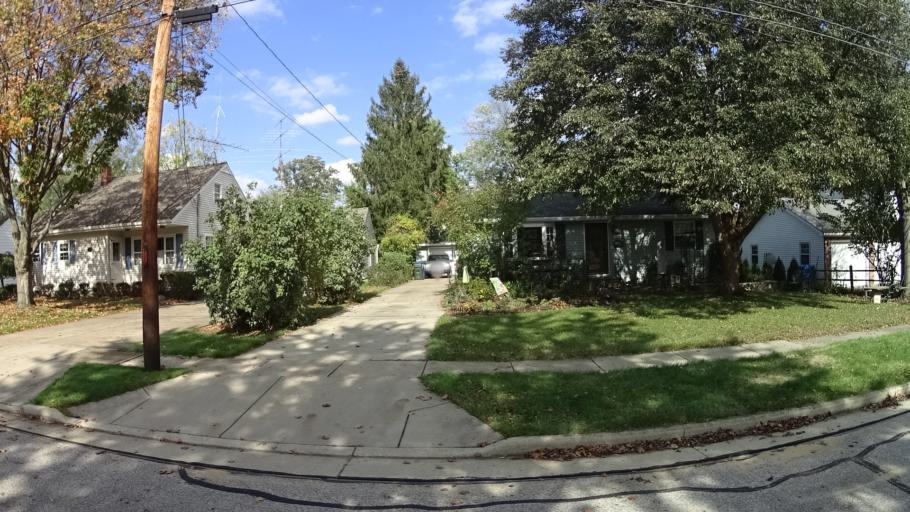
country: US
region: Ohio
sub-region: Lorain County
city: Grafton
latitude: 41.2698
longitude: -82.0531
